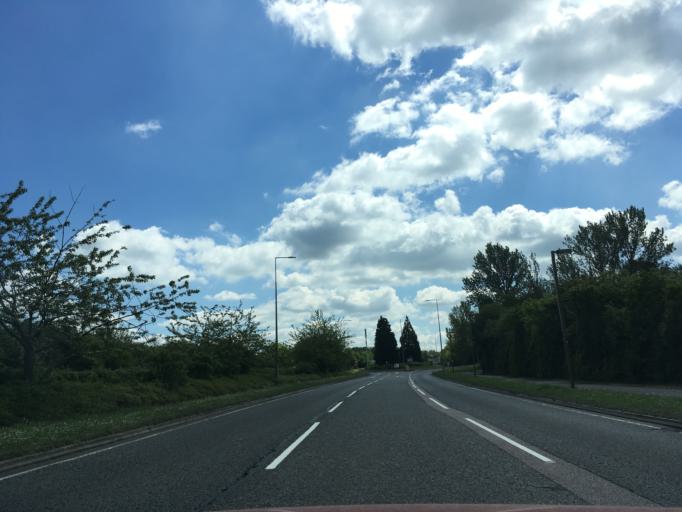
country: GB
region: England
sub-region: Milton Keynes
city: Simpson
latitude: 52.0259
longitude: -0.7048
